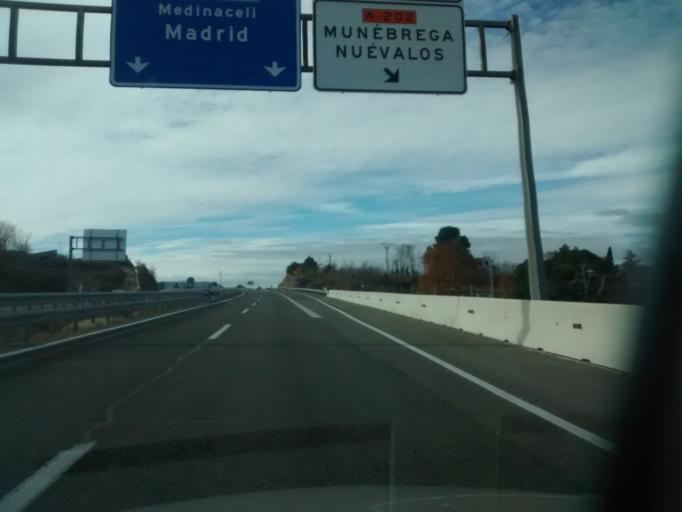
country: ES
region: Aragon
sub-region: Provincia de Zaragoza
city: Paracuellos de Jiloca
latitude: 41.3298
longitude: -1.6603
